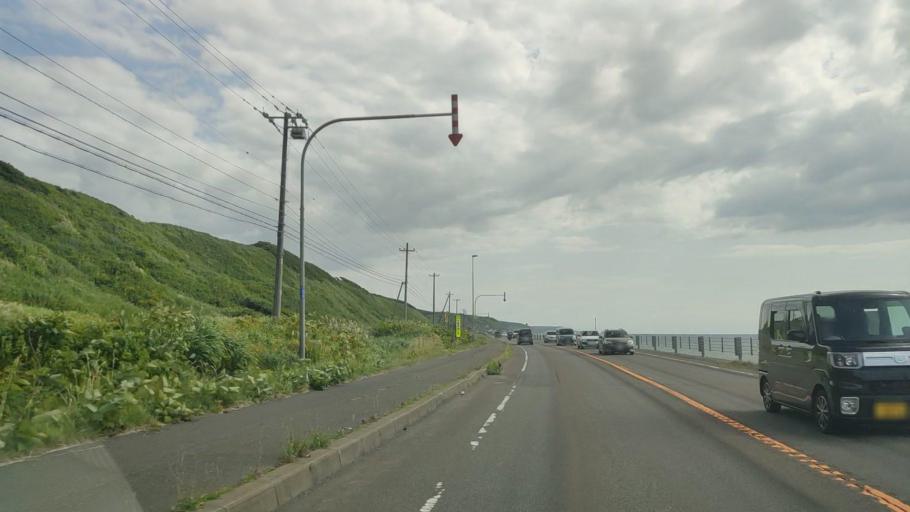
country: JP
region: Hokkaido
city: Rumoi
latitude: 44.2129
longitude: 141.6564
